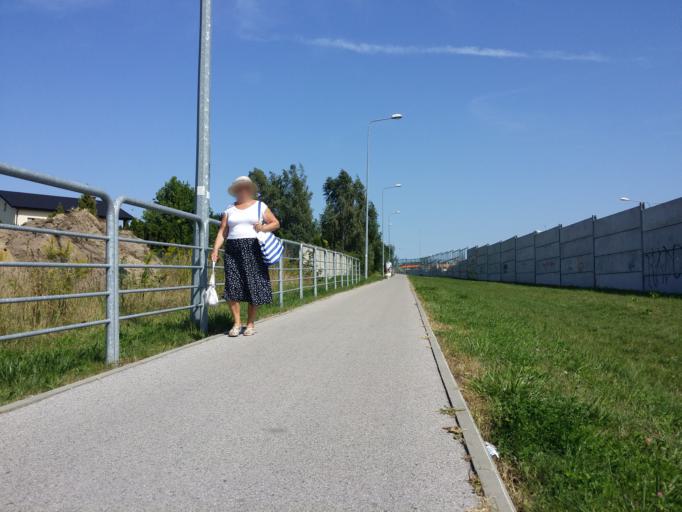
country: PL
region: Masovian Voivodeship
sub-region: Powiat radomski
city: Trablice
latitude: 51.3683
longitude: 21.1458
